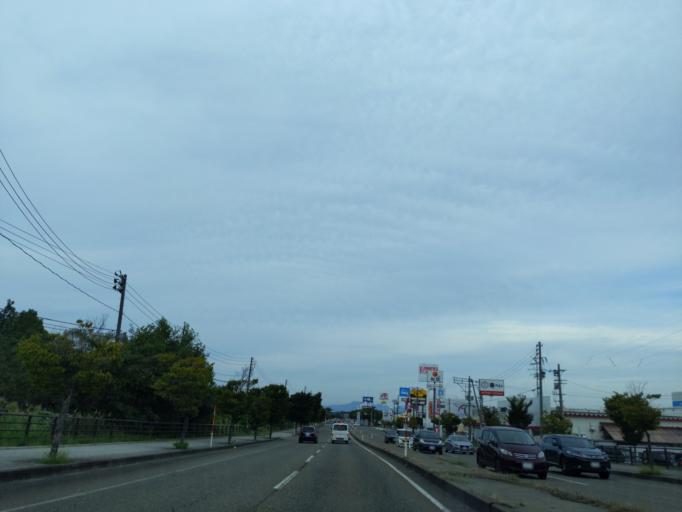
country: JP
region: Niigata
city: Joetsu
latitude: 37.1516
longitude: 138.2491
